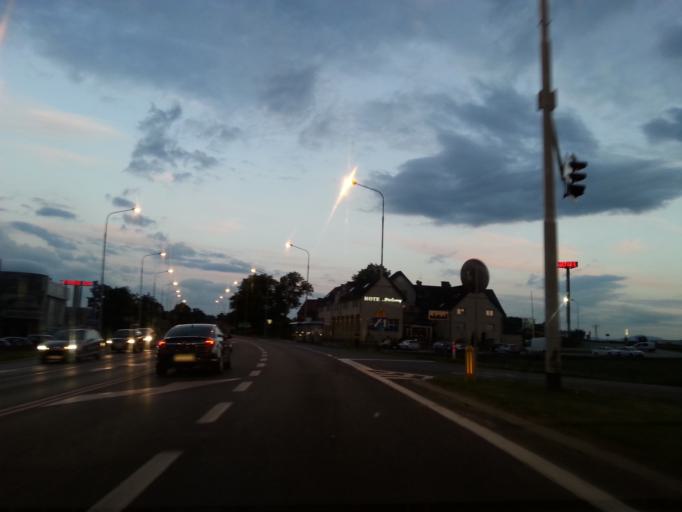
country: PL
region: Lower Silesian Voivodeship
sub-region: Powiat wroclawski
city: Bielany Wroclawskie
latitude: 51.0473
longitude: 16.9706
